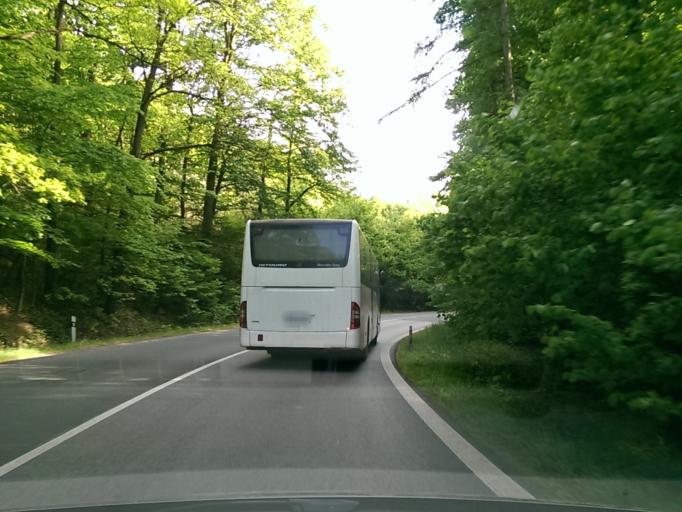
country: CZ
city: Duba
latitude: 50.5301
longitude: 14.5223
